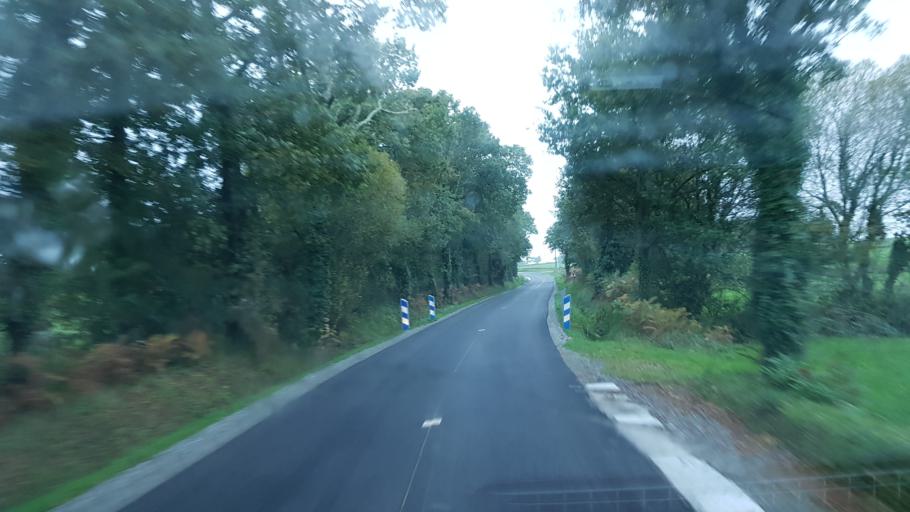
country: FR
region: Brittany
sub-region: Departement du Morbihan
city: Trefflean
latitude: 47.6537
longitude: -2.6293
